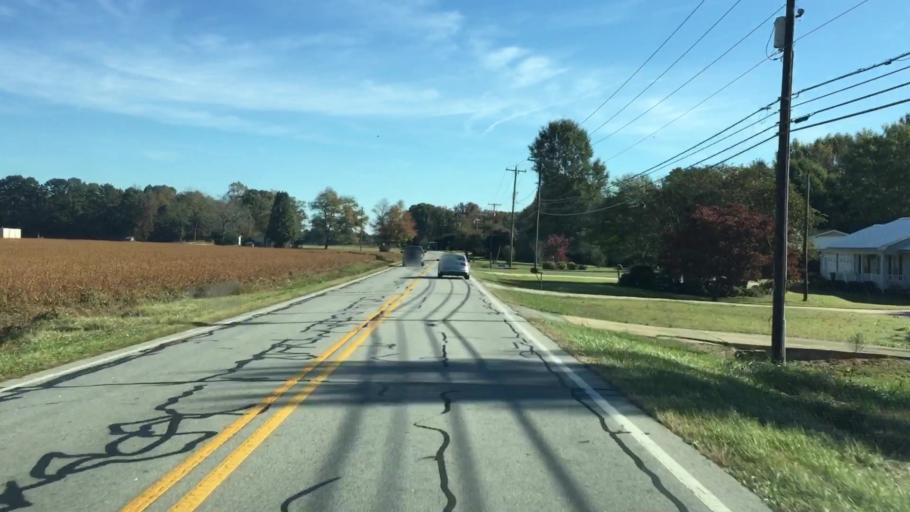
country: US
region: North Carolina
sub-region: Rowan County
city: China Grove
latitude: 35.6548
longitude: -80.5689
